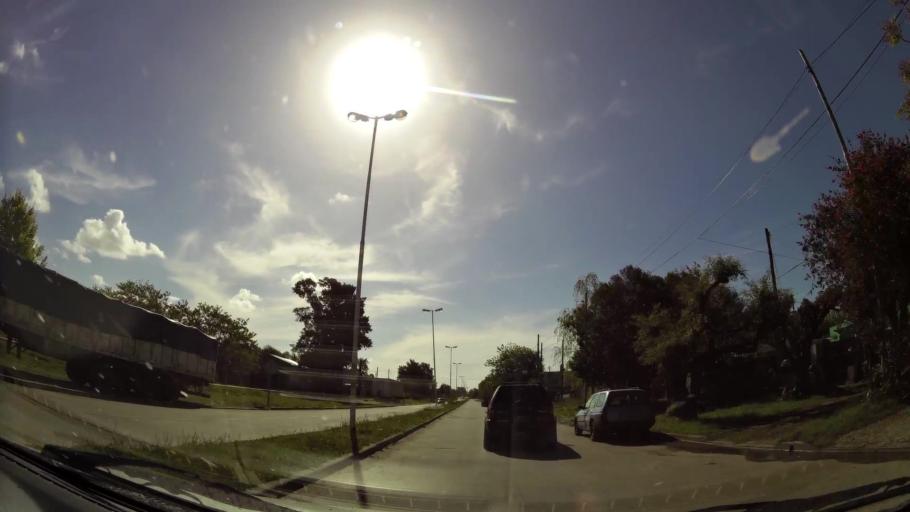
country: AR
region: Buenos Aires
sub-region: Partido de Quilmes
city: Quilmes
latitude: -34.8062
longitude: -58.2257
